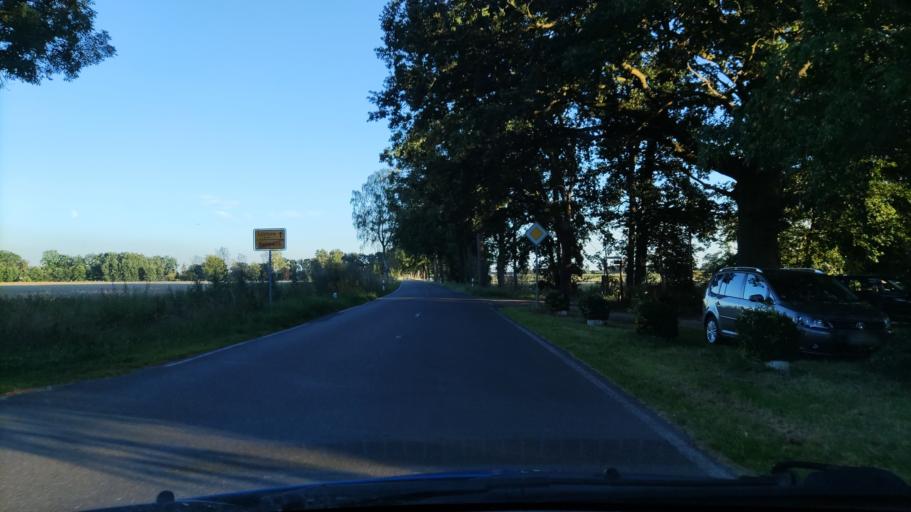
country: DE
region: Lower Saxony
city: Luechow
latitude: 52.9994
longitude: 11.1523
